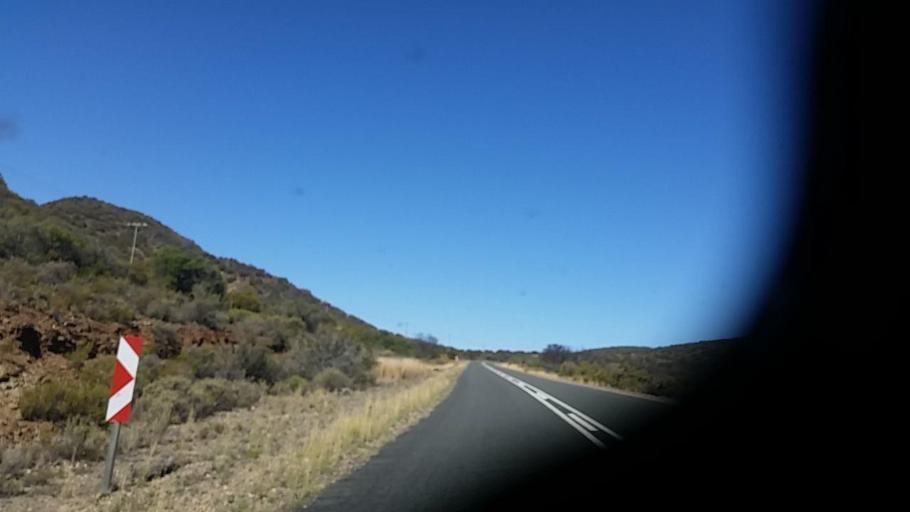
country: ZA
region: Eastern Cape
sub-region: Cacadu District Municipality
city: Willowmore
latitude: -33.4878
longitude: 23.0994
